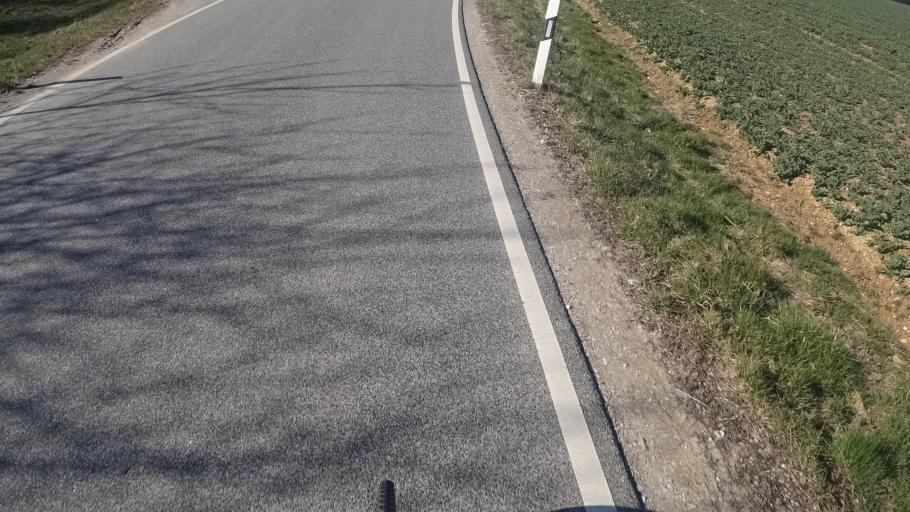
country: DE
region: Rheinland-Pfalz
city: Mengerschied
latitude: 49.9240
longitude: 7.5077
